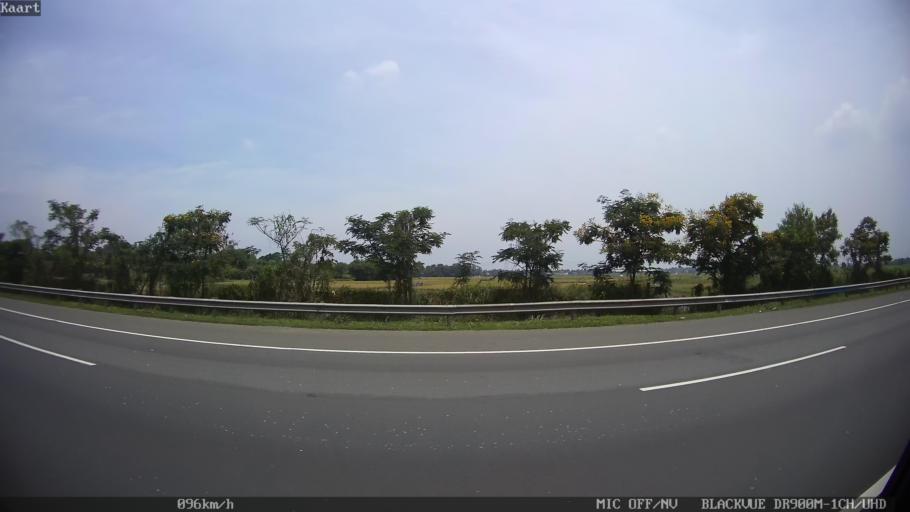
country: ID
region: West Java
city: Kresek
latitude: -6.1771
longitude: 106.3804
